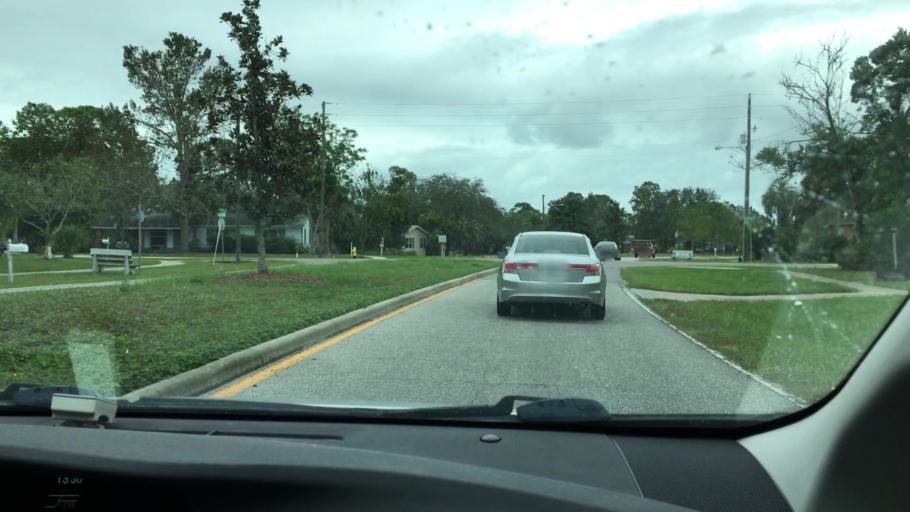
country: US
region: Florida
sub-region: Volusia County
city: Deltona
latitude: 28.8965
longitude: -81.2305
